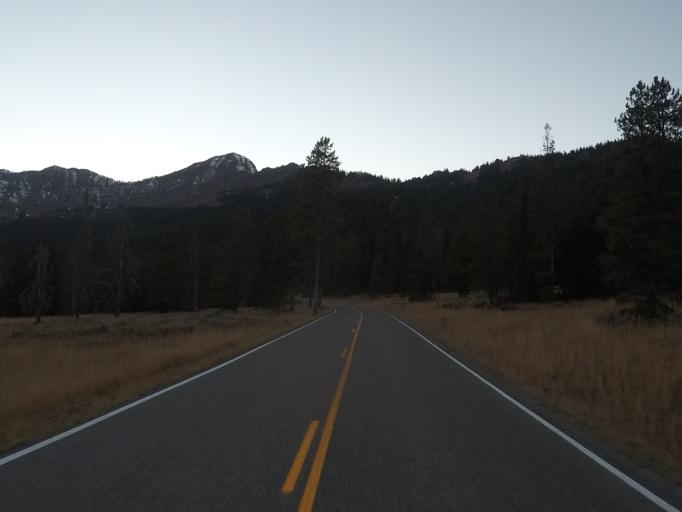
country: US
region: Montana
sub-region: Stillwater County
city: Absarokee
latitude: 45.0051
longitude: -110.0404
